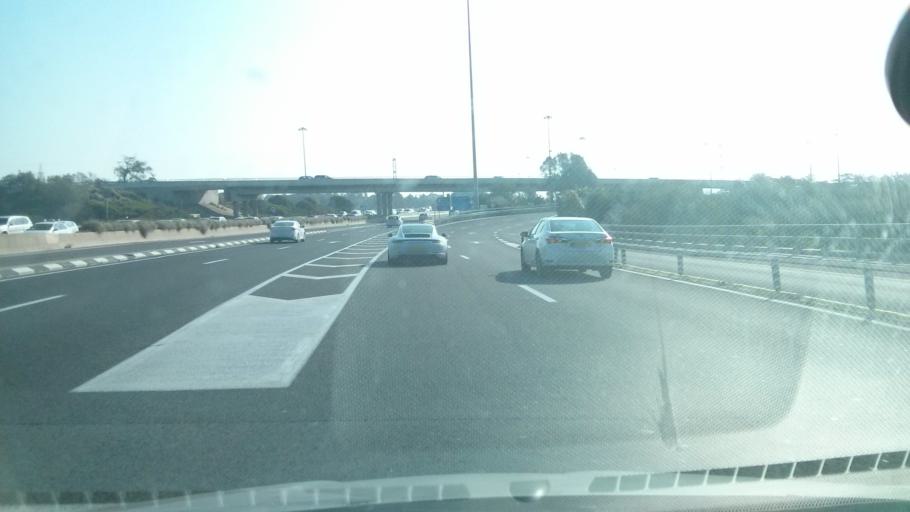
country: IL
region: Tel Aviv
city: Herzliyya
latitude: 32.1402
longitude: 34.8068
